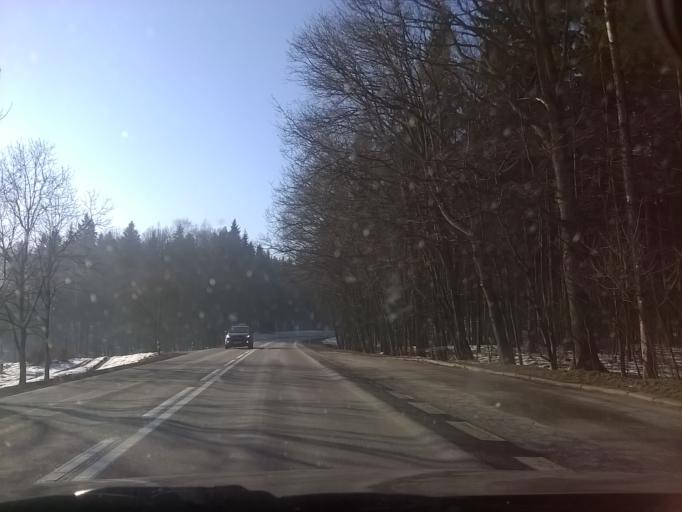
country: PL
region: Warmian-Masurian Voivodeship
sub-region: Powiat olsztynski
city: Biskupiec
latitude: 53.8400
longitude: 21.1168
